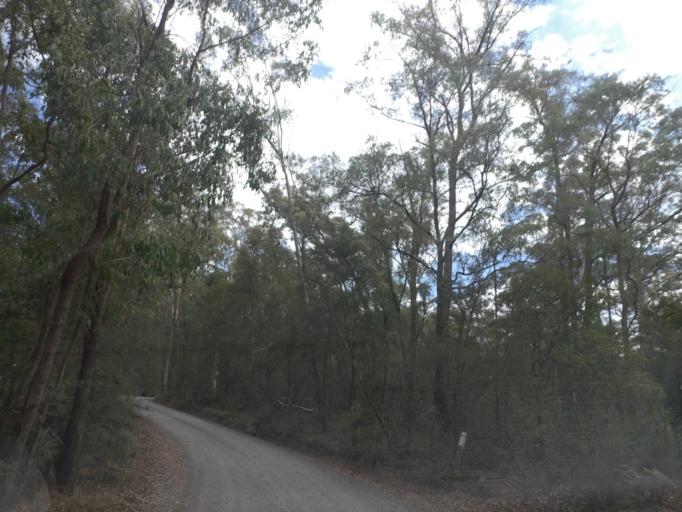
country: AU
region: Victoria
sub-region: Murrindindi
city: Alexandra
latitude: -37.3788
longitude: 145.7593
